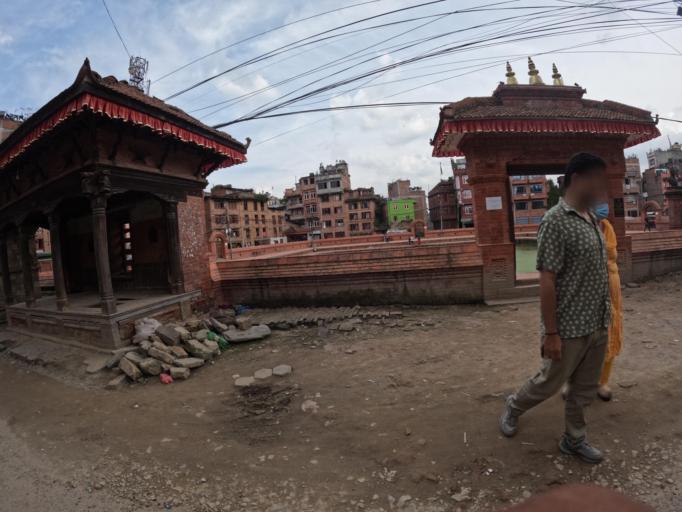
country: NP
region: Central Region
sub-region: Bagmati Zone
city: Bhaktapur
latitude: 27.6788
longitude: 85.3857
